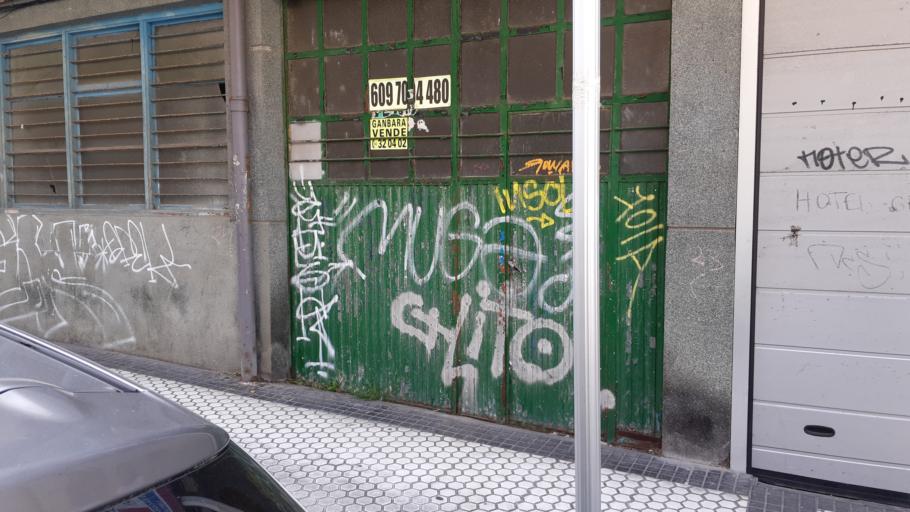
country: ES
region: Basque Country
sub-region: Provincia de Guipuzcoa
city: San Sebastian
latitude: 43.3172
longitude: -1.9725
